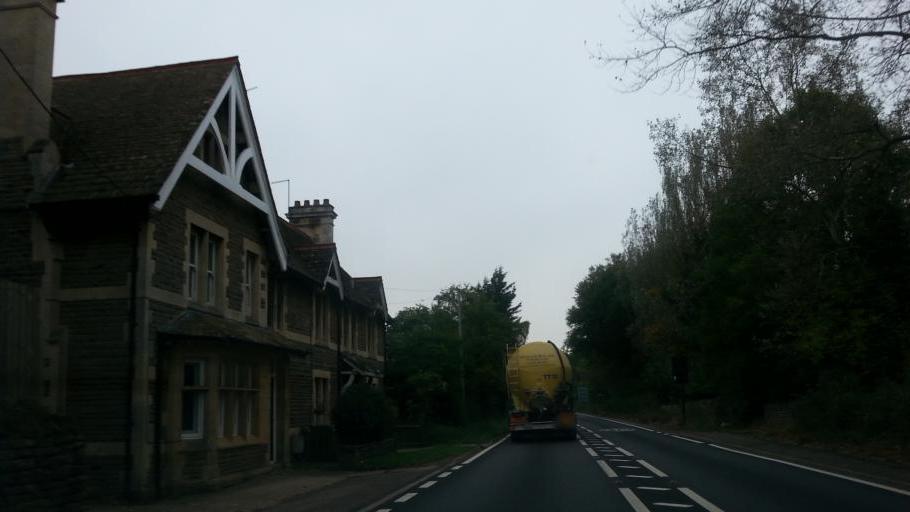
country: GB
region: England
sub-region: Northamptonshire
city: Thrapston
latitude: 52.4211
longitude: -0.4957
